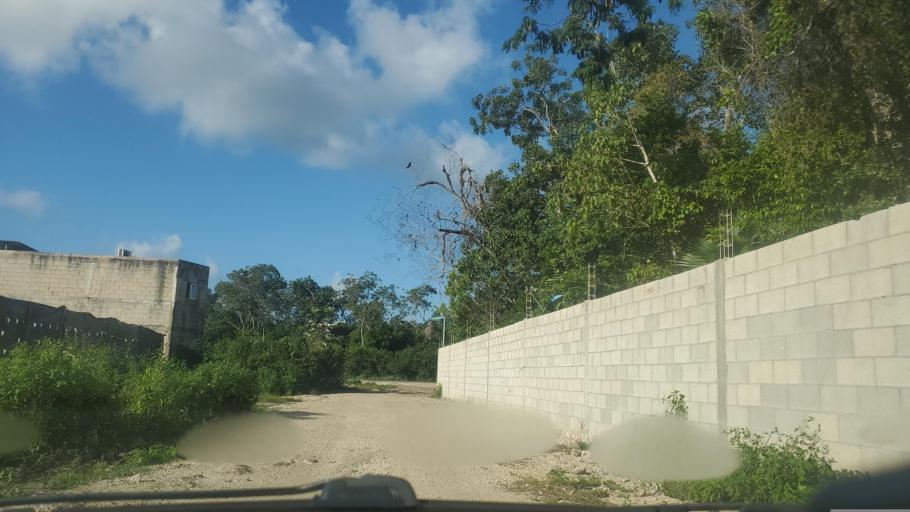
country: MX
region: Quintana Roo
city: Tulum
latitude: 20.2072
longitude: -87.4789
